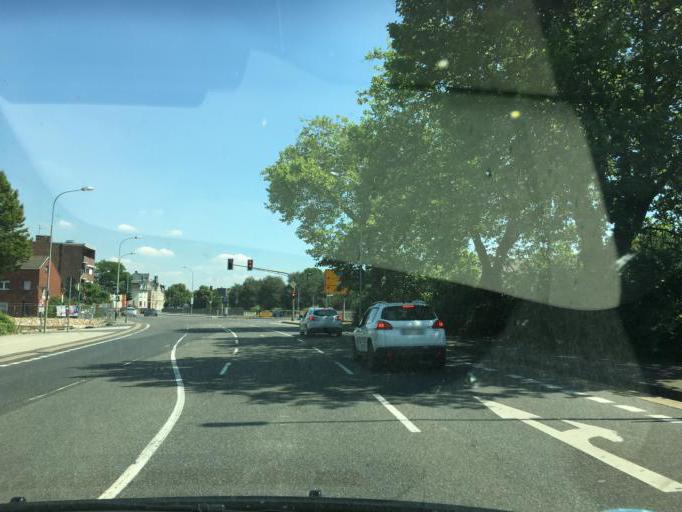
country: DE
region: North Rhine-Westphalia
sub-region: Regierungsbezirk Koln
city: Eschweiler
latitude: 50.8175
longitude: 6.2715
